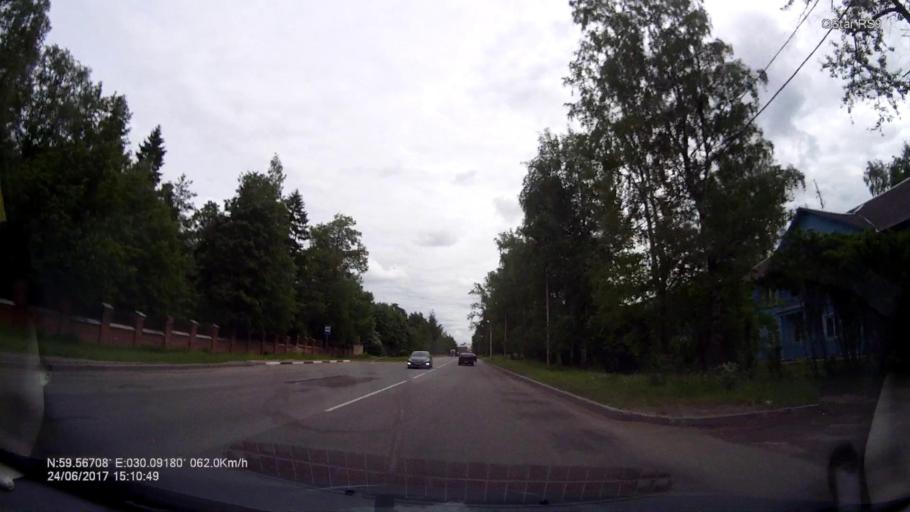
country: RU
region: Leningrad
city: Mariyenburg
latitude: 59.5669
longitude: 30.0923
